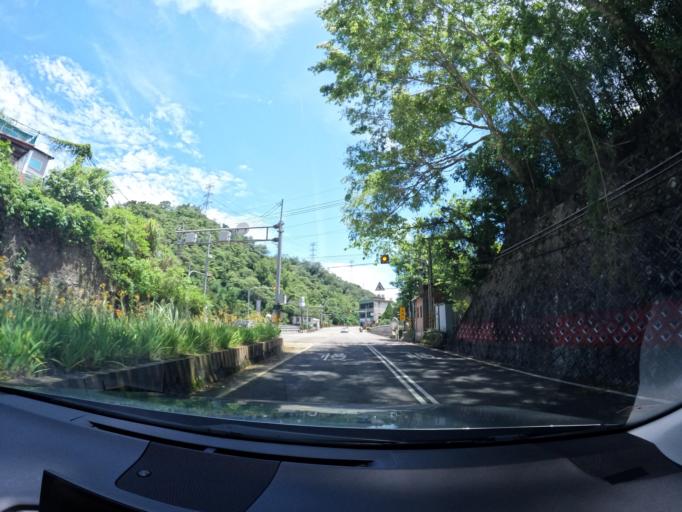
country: TW
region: Taiwan
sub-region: Miaoli
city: Miaoli
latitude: 24.5794
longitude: 120.9403
